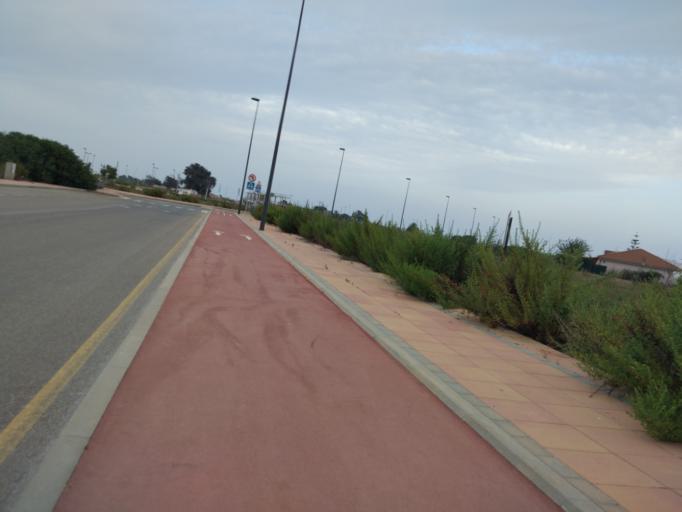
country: ES
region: Murcia
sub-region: Murcia
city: Los Alcazares
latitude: 37.7217
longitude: -0.8646
